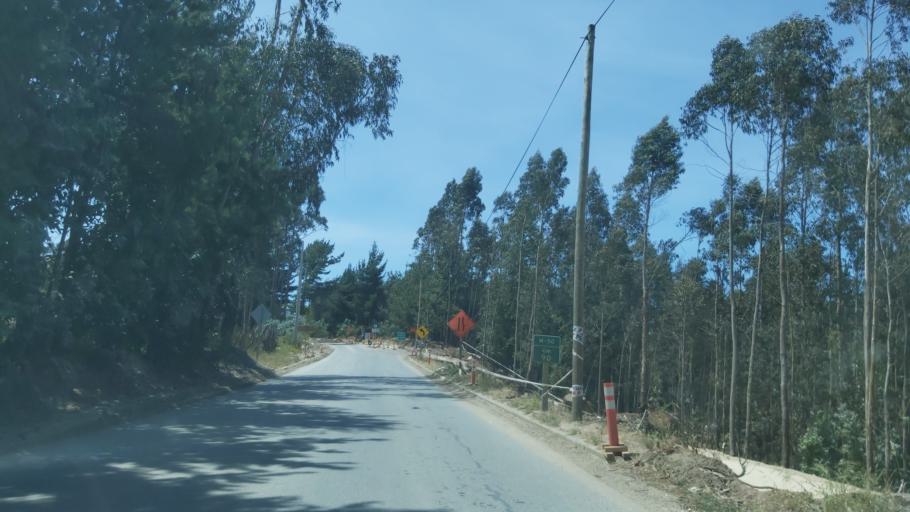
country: CL
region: Maule
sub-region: Provincia de Talca
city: Constitucion
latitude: -35.4399
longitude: -72.4559
